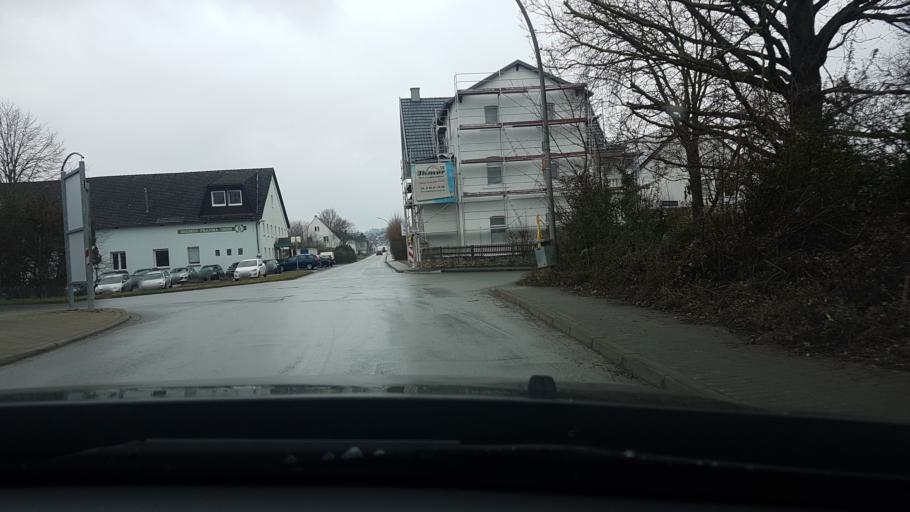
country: DE
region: North Rhine-Westphalia
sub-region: Regierungsbezirk Detmold
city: Willebadessen
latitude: 51.5256
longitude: 9.0354
